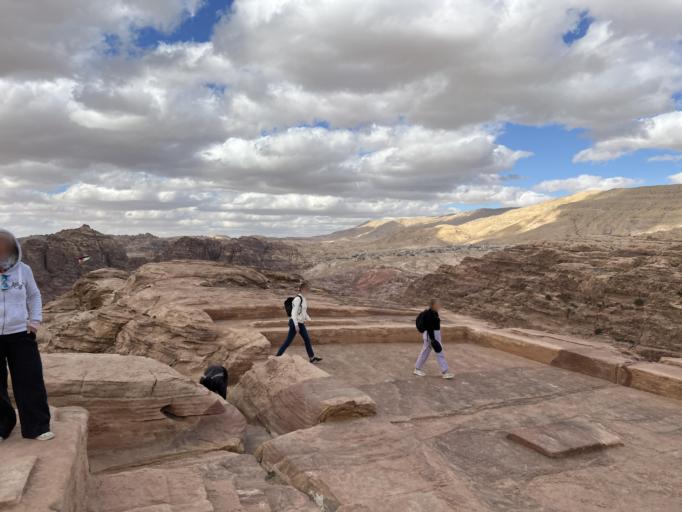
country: JO
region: Ma'an
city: Petra
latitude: 30.3214
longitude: 35.4470
